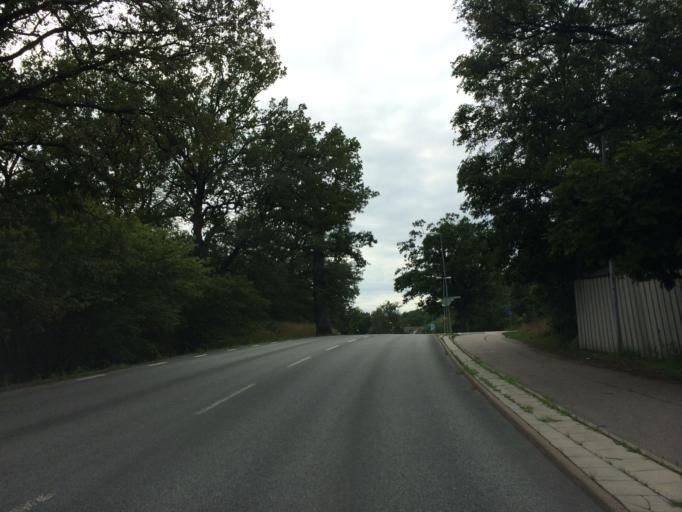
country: SE
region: Stockholm
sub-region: Sollentuna Kommun
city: Sollentuna
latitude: 59.4583
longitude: 17.9080
